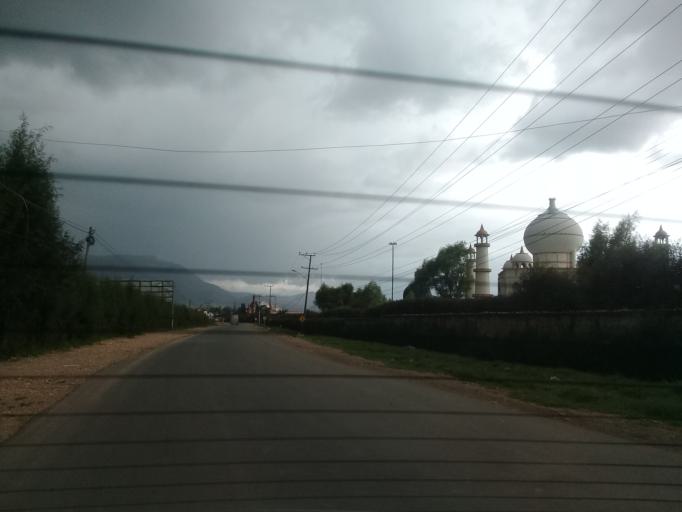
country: CO
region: Cundinamarca
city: Sopo
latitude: 4.9499
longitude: -73.9627
